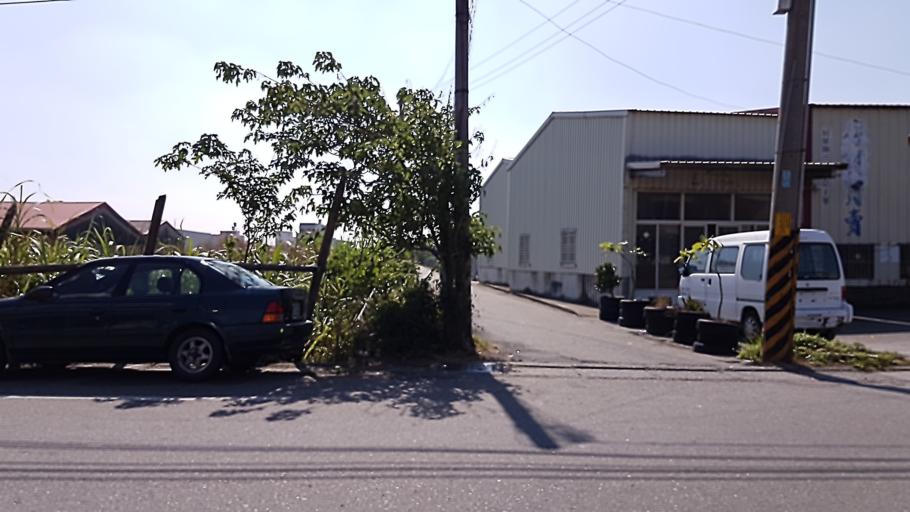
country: TW
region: Taiwan
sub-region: Changhua
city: Chang-hua
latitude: 24.0813
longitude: 120.5016
